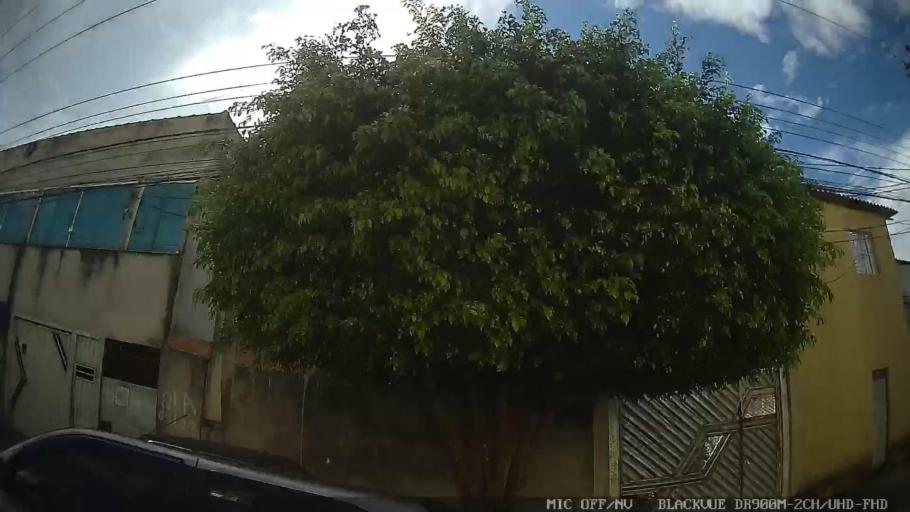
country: BR
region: Sao Paulo
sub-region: Suzano
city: Suzano
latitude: -23.5544
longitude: -46.2477
